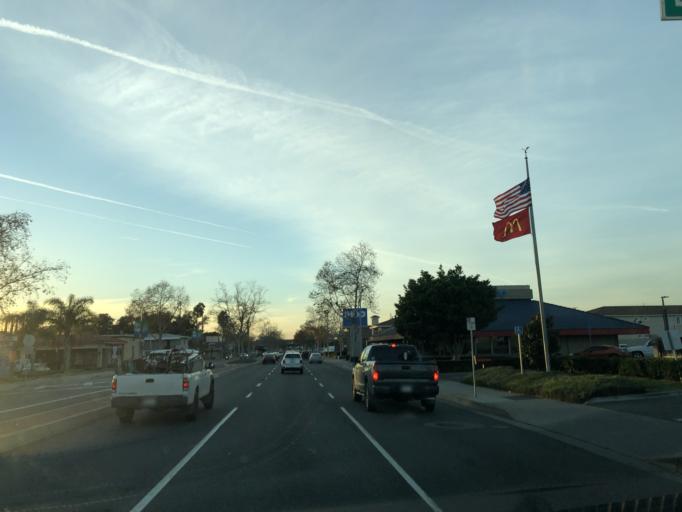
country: US
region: California
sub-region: Orange County
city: Santa Ana
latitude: 33.7600
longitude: -117.8563
